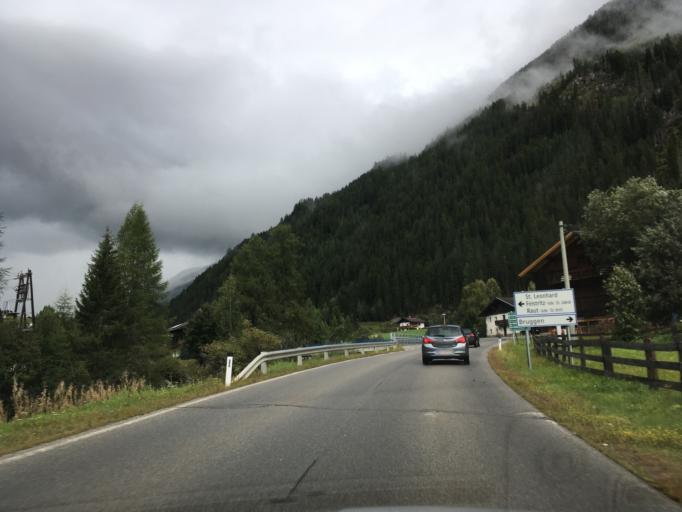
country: AT
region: Tyrol
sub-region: Politischer Bezirk Lienz
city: Innervillgraten
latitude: 46.9147
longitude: 12.3777
